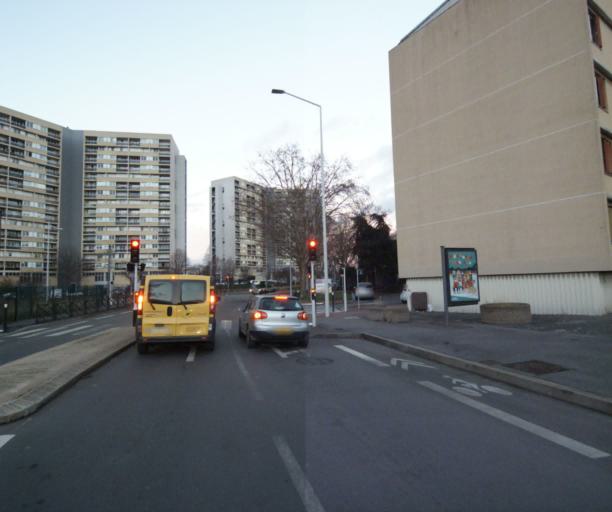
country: FR
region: Ile-de-France
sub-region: Departement des Hauts-de-Seine
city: Nanterre
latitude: 48.8981
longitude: 2.2066
